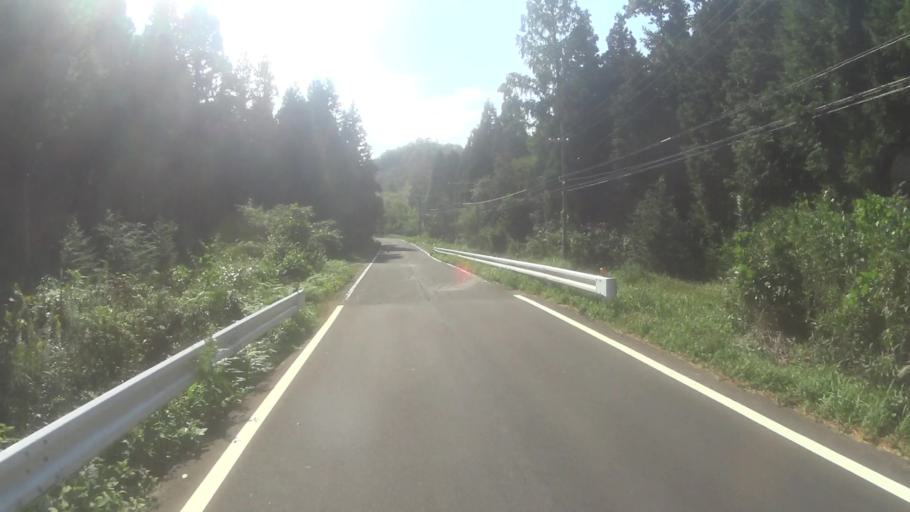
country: JP
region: Kyoto
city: Miyazu
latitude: 35.6870
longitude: 135.1136
